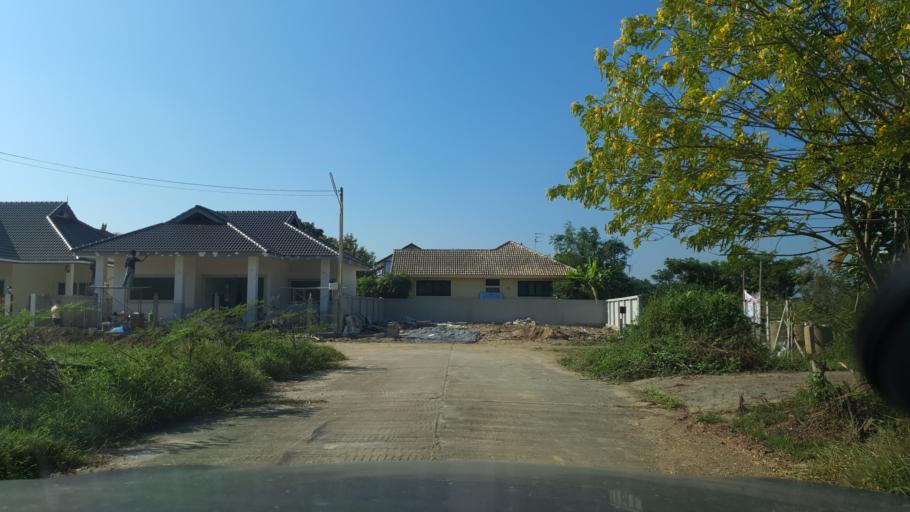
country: TH
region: Chiang Mai
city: Saraphi
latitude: 18.7263
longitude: 99.0598
